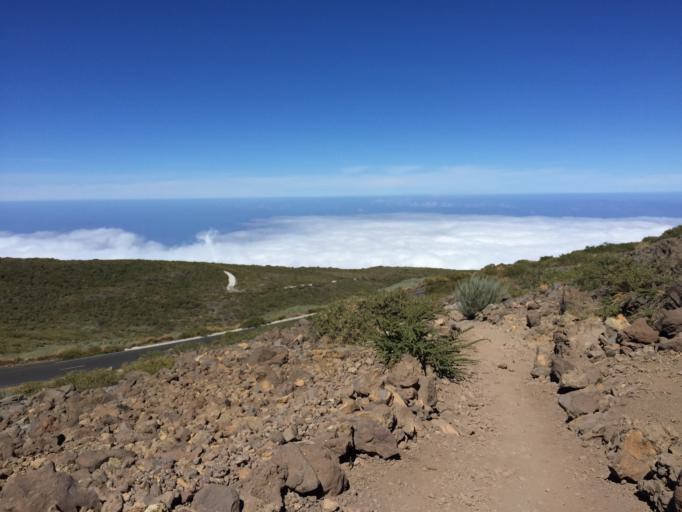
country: ES
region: Canary Islands
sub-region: Provincia de Santa Cruz de Tenerife
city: Barlovento
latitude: 28.7592
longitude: -17.8598
